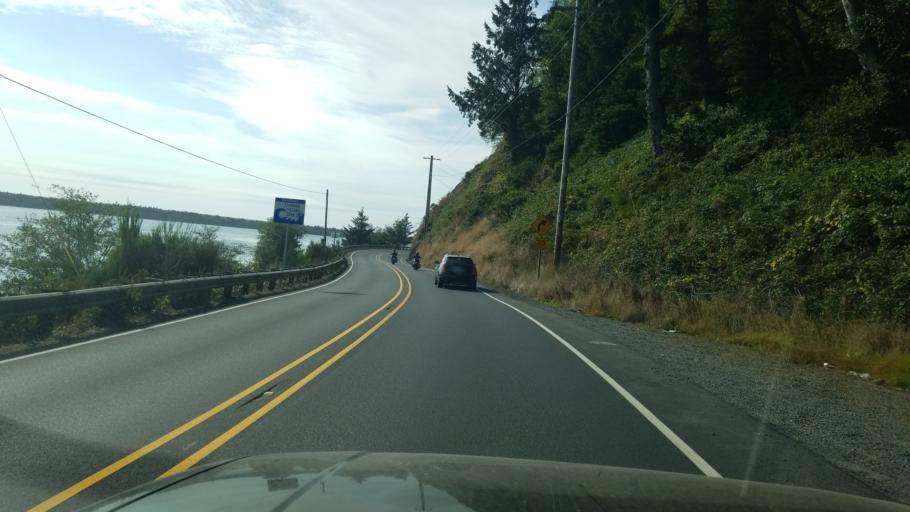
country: US
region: Oregon
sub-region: Tillamook County
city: Rockaway Beach
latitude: 45.5603
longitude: -123.9315
